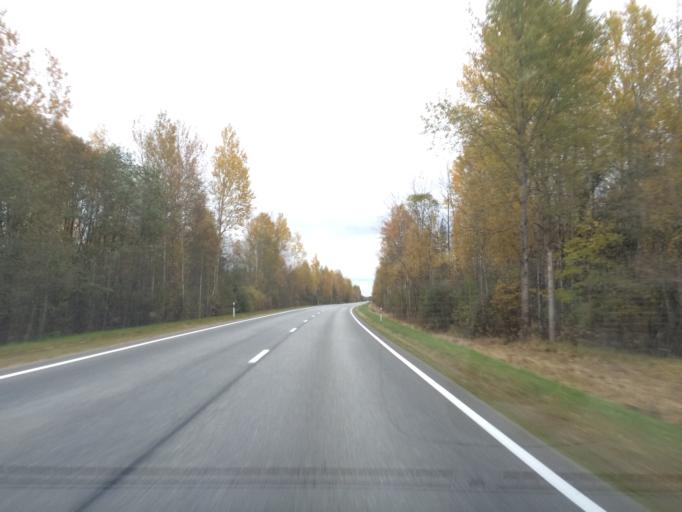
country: LV
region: Livani
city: Livani
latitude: 56.5286
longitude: 26.3939
